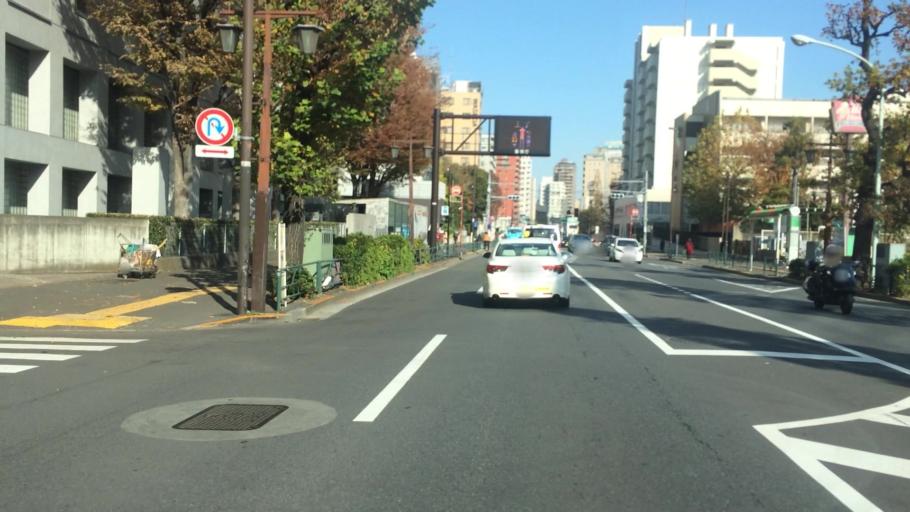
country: JP
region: Tokyo
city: Tokyo
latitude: 35.7053
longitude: 139.7087
